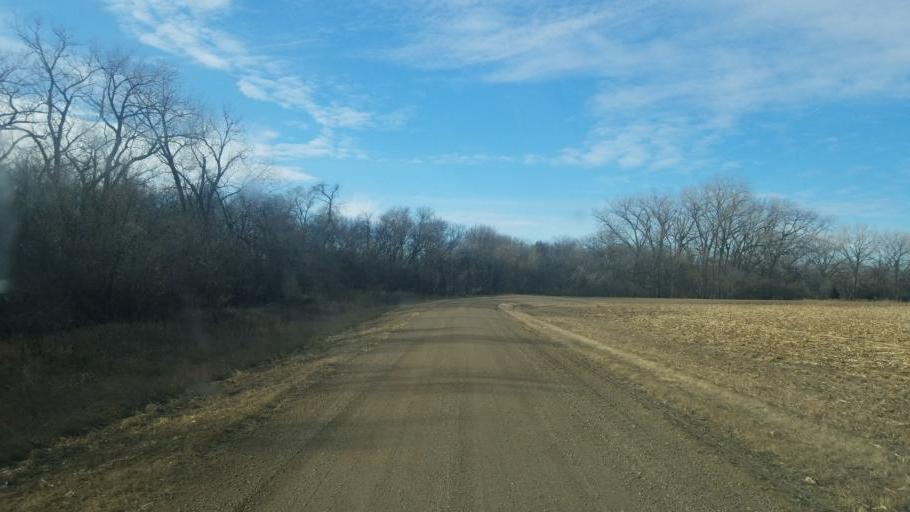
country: US
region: South Dakota
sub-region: Charles Mix County
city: Wagner
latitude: 42.9516
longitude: -98.4546
